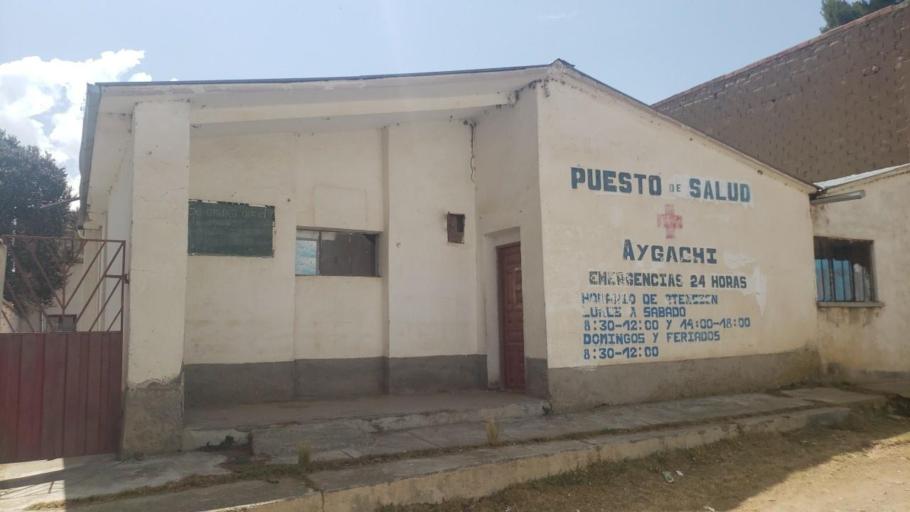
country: BO
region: La Paz
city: Batallas
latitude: -16.3773
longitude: -68.5952
